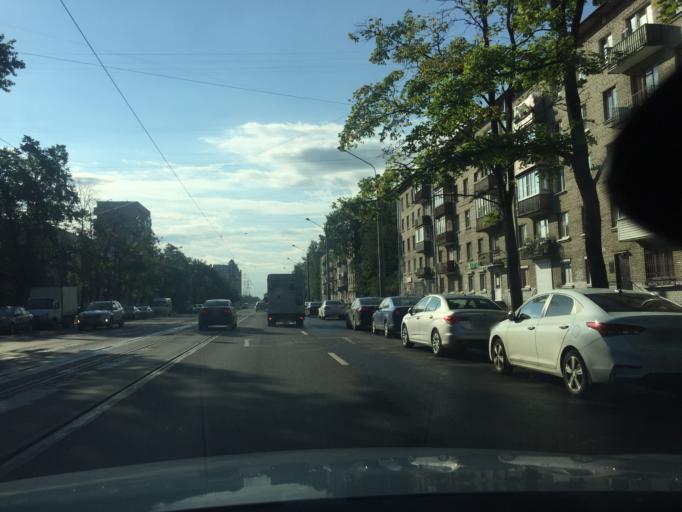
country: RU
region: St.-Petersburg
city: Kupchino
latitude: 59.8382
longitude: 30.3390
